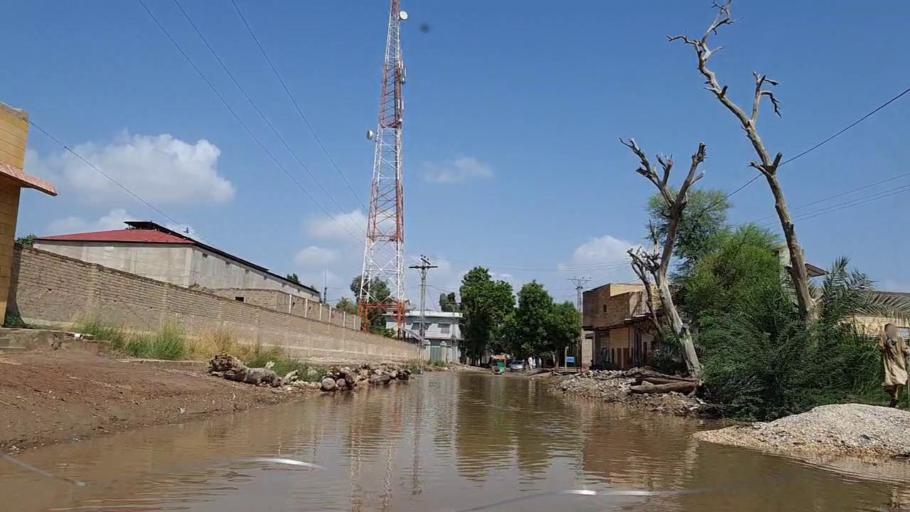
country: PK
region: Sindh
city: Pad Idan
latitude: 26.7756
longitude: 68.2968
